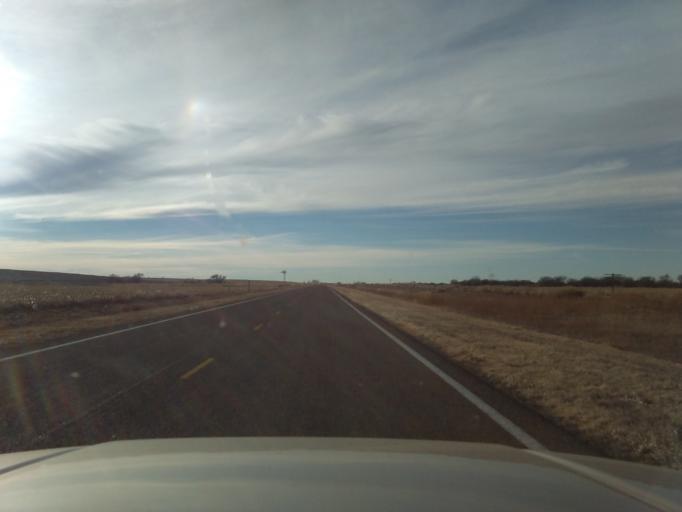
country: US
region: Kansas
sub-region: Norton County
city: Norton
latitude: 39.7557
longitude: -100.1206
